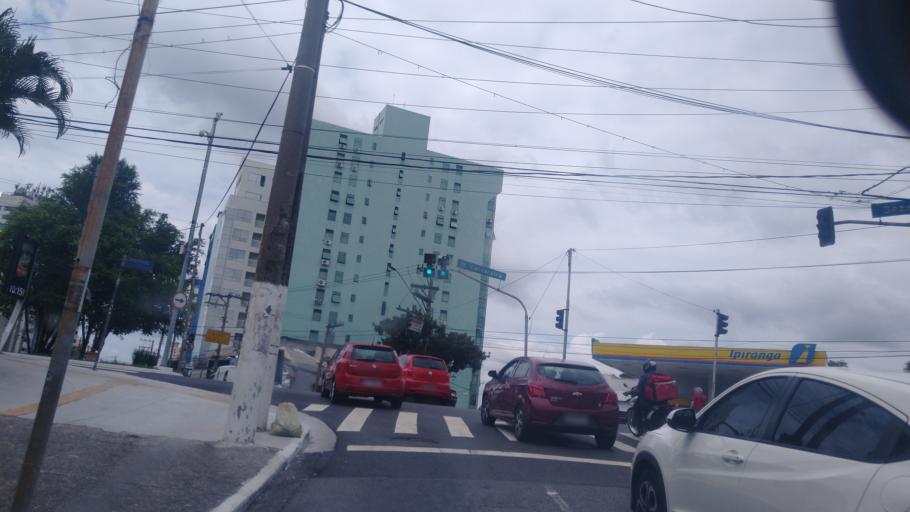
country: BR
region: Sao Paulo
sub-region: Sao Paulo
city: Sao Paulo
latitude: -23.4771
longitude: -46.6102
